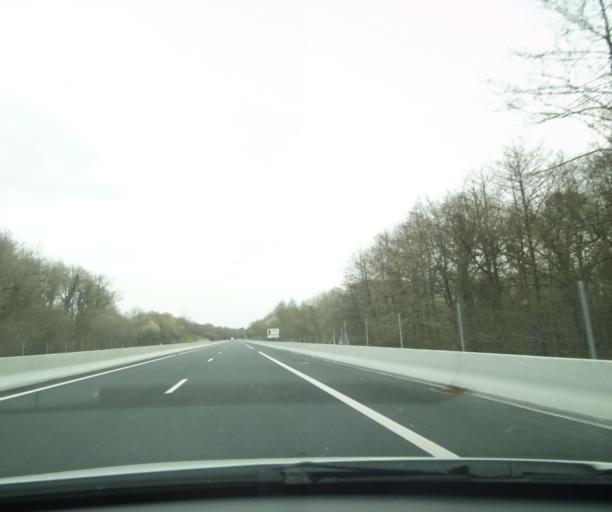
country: FR
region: Aquitaine
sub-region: Departement des Pyrenees-Atlantiques
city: Mouguerre
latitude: 43.4556
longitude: -1.4088
